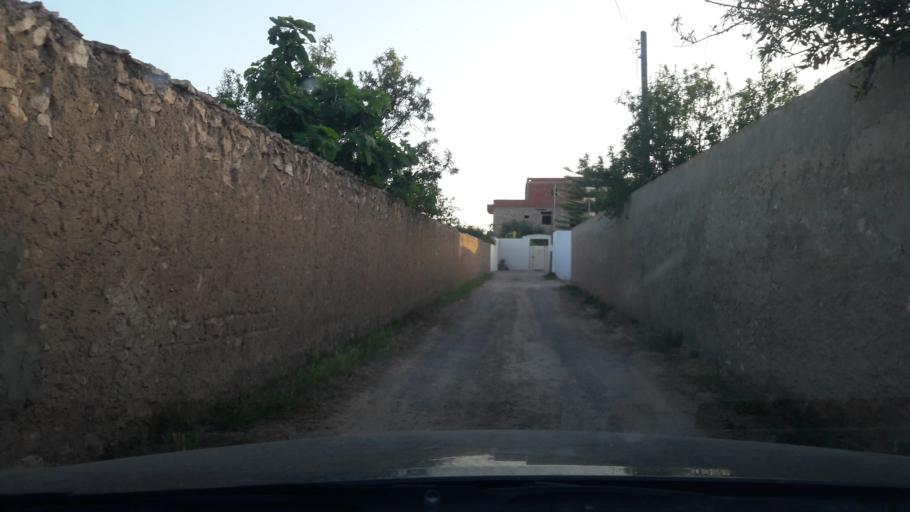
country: TN
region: Safaqis
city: Al Qarmadah
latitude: 34.7914
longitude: 10.7532
